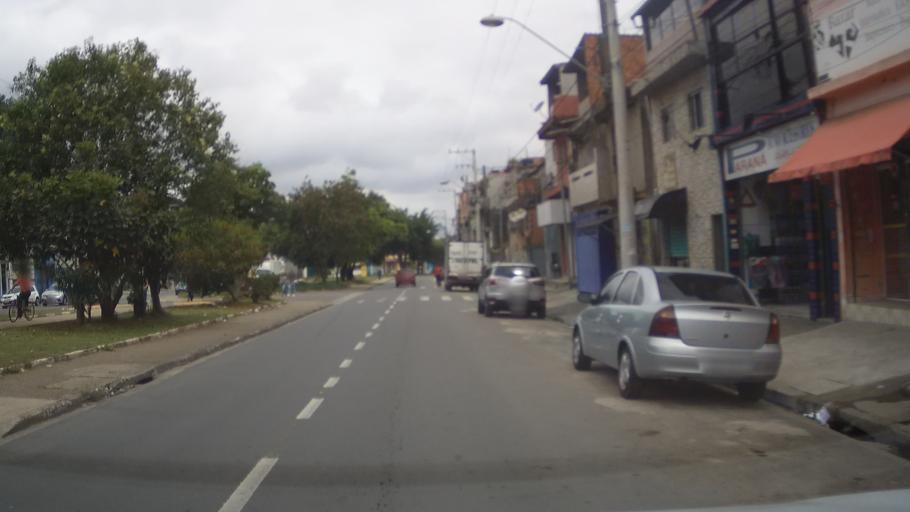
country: BR
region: Sao Paulo
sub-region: Itaquaquecetuba
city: Itaquaquecetuba
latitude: -23.4388
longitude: -46.3819
